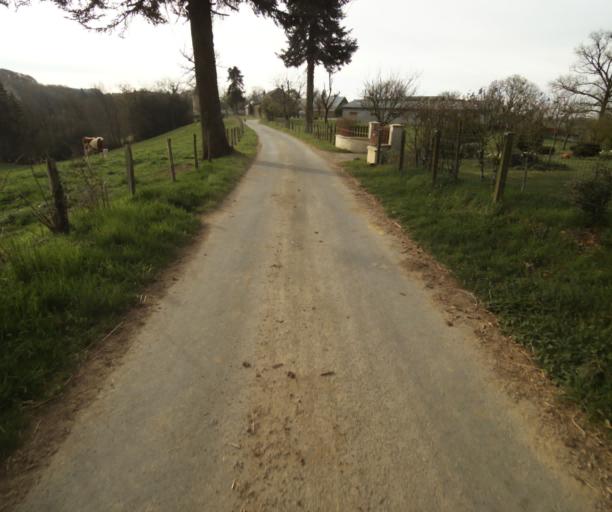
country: FR
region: Limousin
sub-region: Departement de la Correze
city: Chamboulive
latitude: 45.4516
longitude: 1.7568
